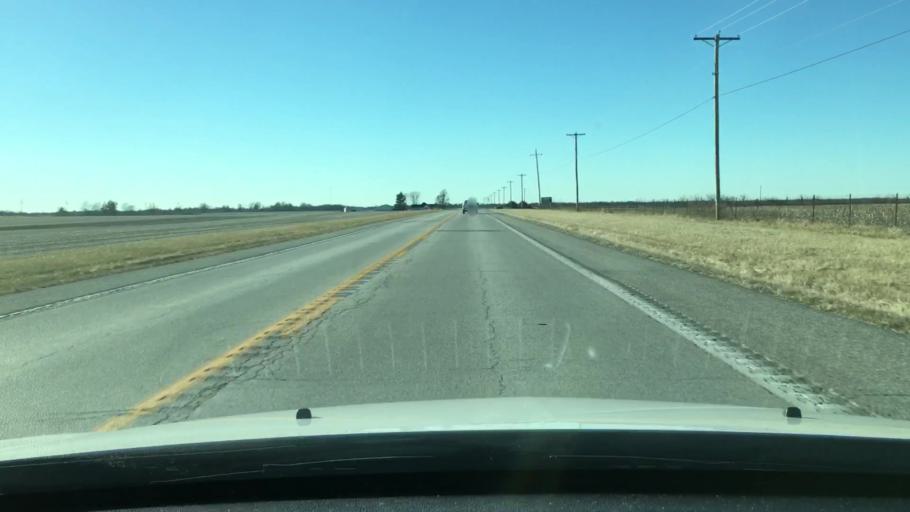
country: US
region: Missouri
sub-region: Audrain County
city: Vandalia
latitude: 39.3458
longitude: -91.3571
